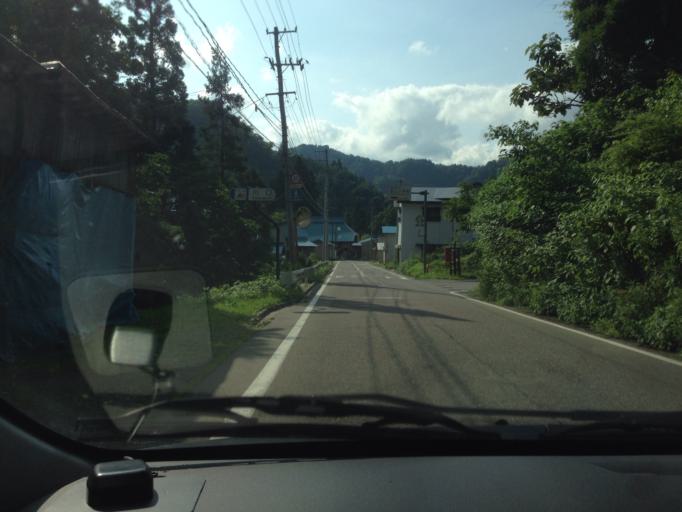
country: JP
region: Fukushima
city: Kitakata
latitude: 37.4504
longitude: 139.5250
